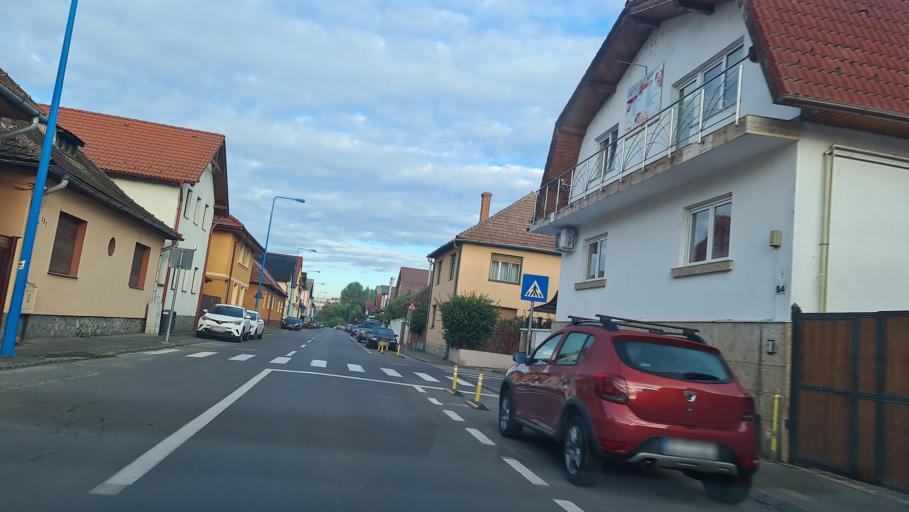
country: RO
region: Brasov
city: Brasov
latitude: 45.6626
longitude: 25.5963
